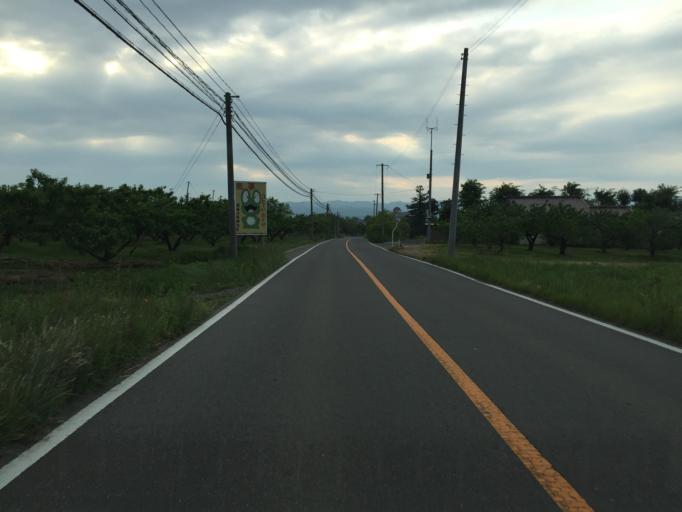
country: JP
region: Fukushima
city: Yanagawamachi-saiwaicho
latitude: 37.8756
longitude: 140.5587
